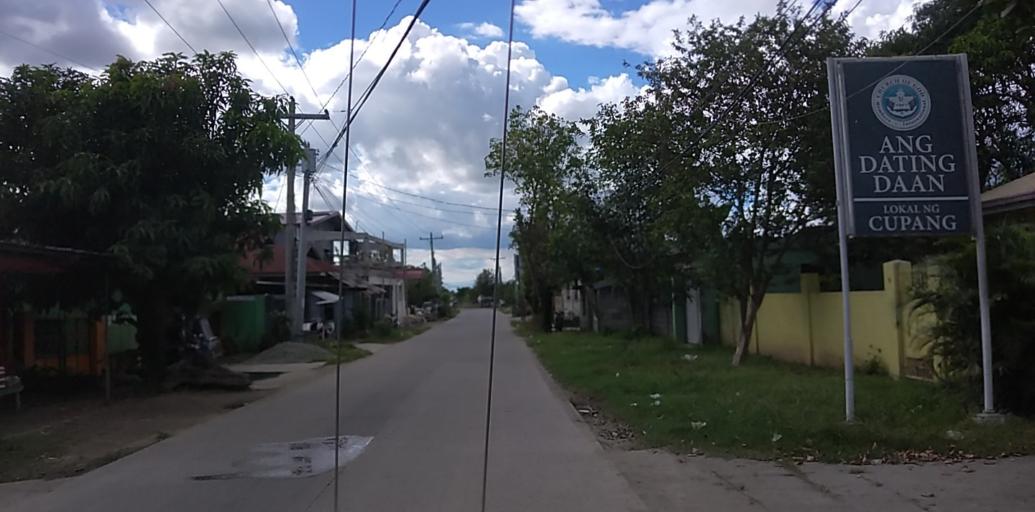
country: PH
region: Central Luzon
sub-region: Province of Pampanga
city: Arayat
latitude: 15.1403
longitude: 120.7798
